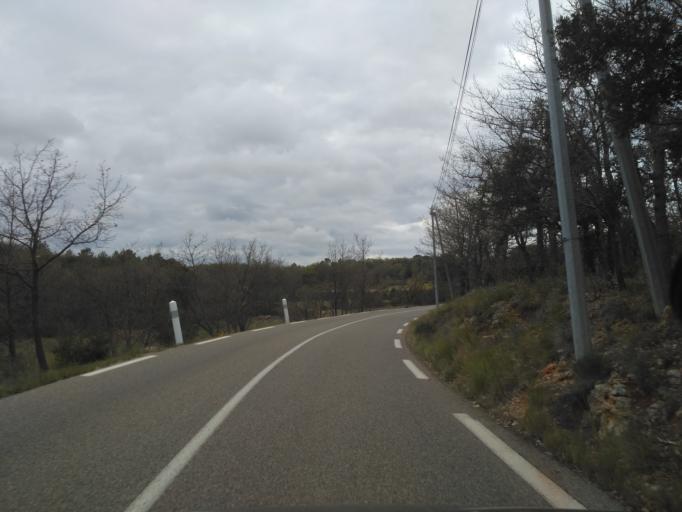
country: FR
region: Provence-Alpes-Cote d'Azur
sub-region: Departement du Var
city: Barjols
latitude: 43.6145
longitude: 5.9480
